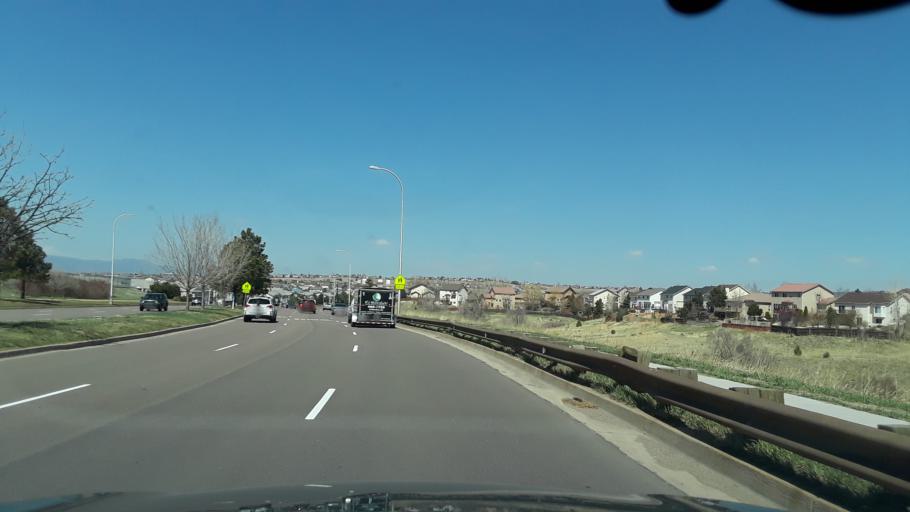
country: US
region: Colorado
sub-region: El Paso County
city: Cimarron Hills
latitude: 38.9263
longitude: -104.7386
